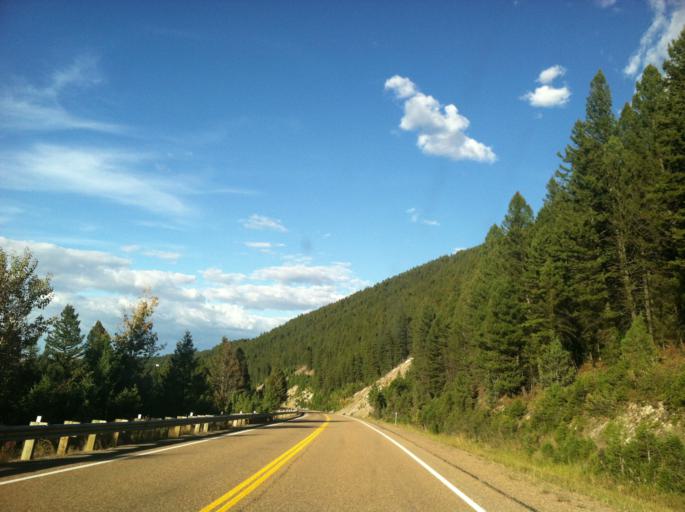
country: US
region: Montana
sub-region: Granite County
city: Philipsburg
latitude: 46.4513
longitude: -113.2430
